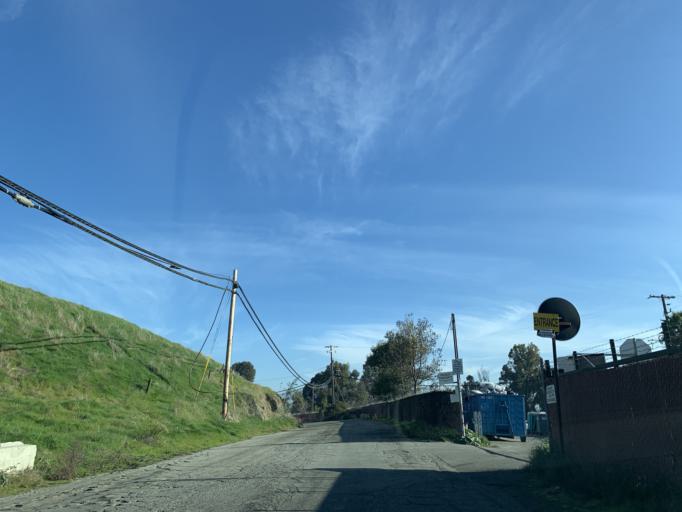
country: US
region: California
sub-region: Santa Clara County
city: Seven Trees
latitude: 37.2834
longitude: -121.8456
